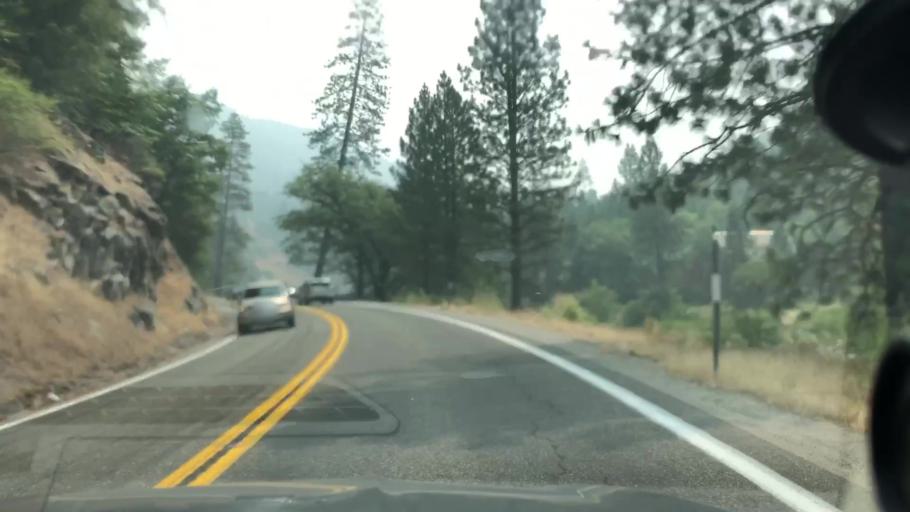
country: US
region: California
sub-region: El Dorado County
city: Pollock Pines
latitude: 38.7736
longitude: -120.3985
